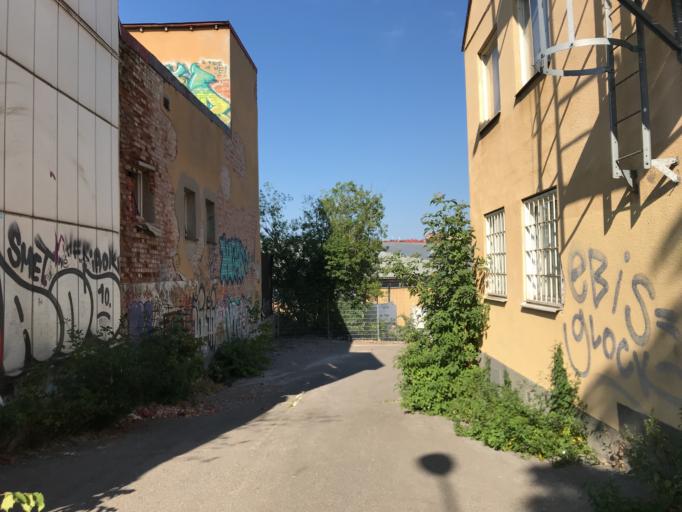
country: SE
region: Stockholm
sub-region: Stockholms Kommun
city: Arsta
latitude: 59.3149
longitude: 18.0202
